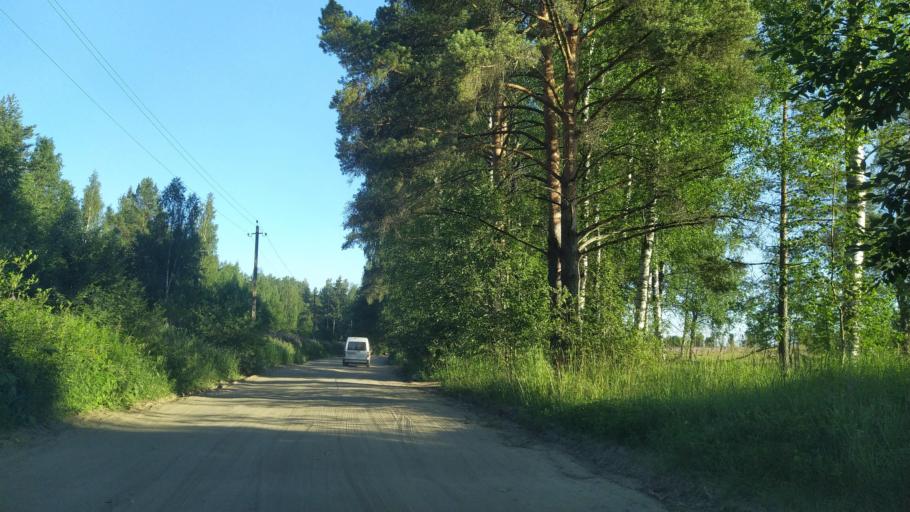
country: RU
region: Leningrad
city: Koltushi
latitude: 59.9097
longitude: 30.7364
